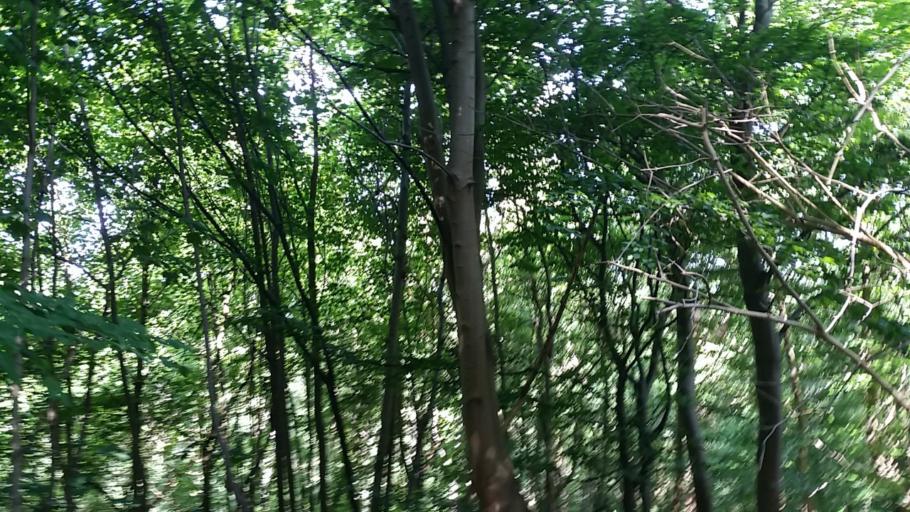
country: DE
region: Schleswig-Holstein
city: Halstenbek
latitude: 53.5608
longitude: 9.7934
